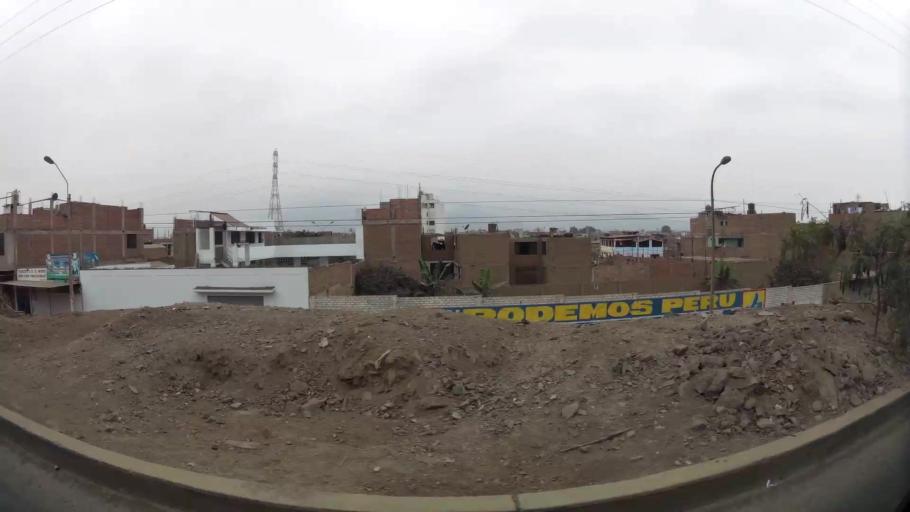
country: PE
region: Lima
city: Ventanilla
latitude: -11.9260
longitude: -77.0819
